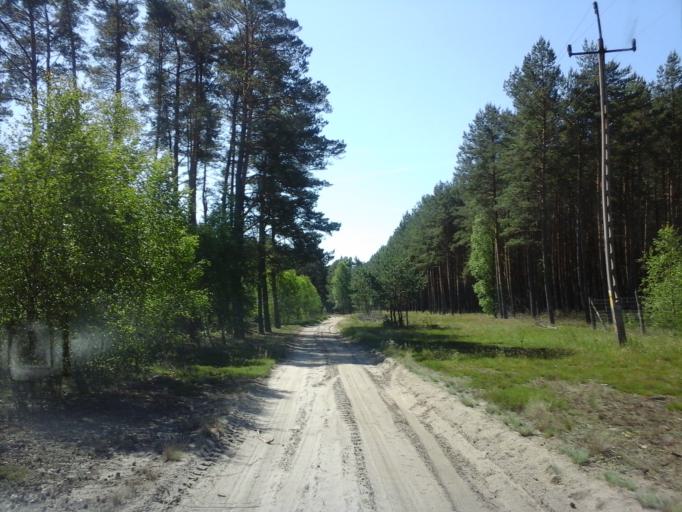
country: PL
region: West Pomeranian Voivodeship
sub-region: Powiat drawski
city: Kalisz Pomorski
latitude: 53.1645
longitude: 15.9814
